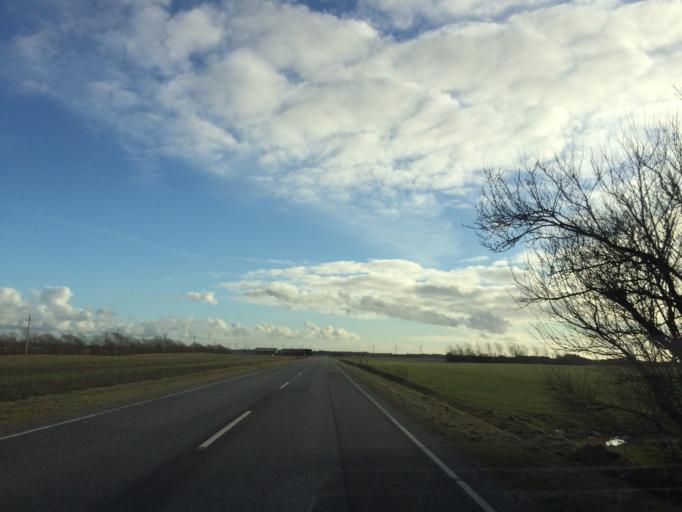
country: DK
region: Central Jutland
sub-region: Lemvig Kommune
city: Lemvig
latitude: 56.4445
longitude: 8.2956
